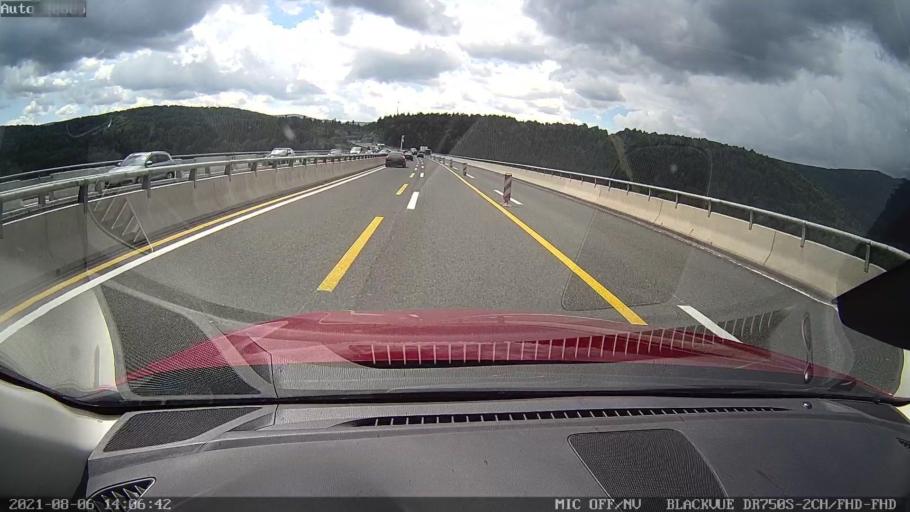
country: HR
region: Primorsko-Goranska
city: Vrbovsko
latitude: 45.3770
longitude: 15.1294
